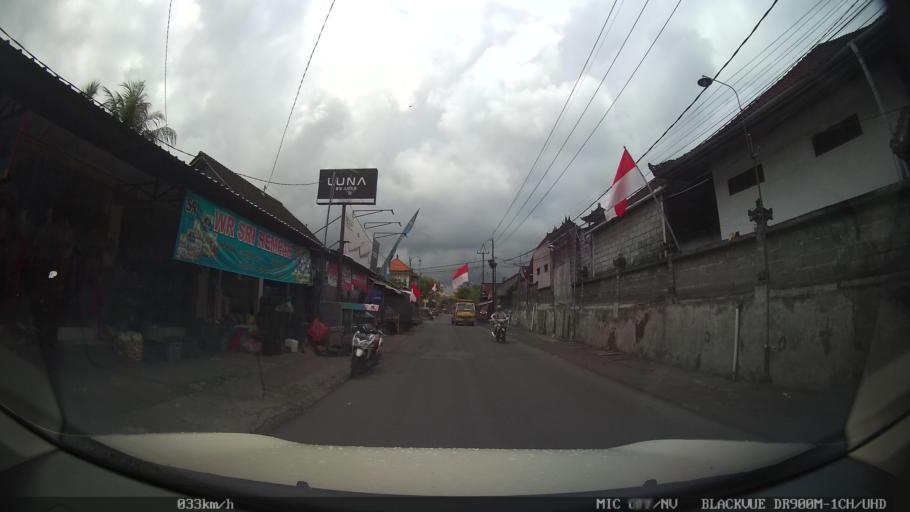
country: ID
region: Bali
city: Banjar Pekenjelodan
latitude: -8.5682
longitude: 115.1818
